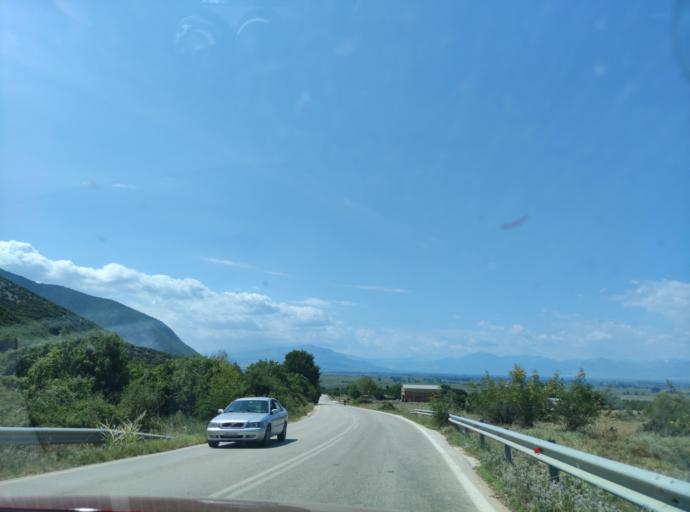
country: GR
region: East Macedonia and Thrace
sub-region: Nomos Kavalas
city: Nikisiani
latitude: 40.9726
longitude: 24.1381
